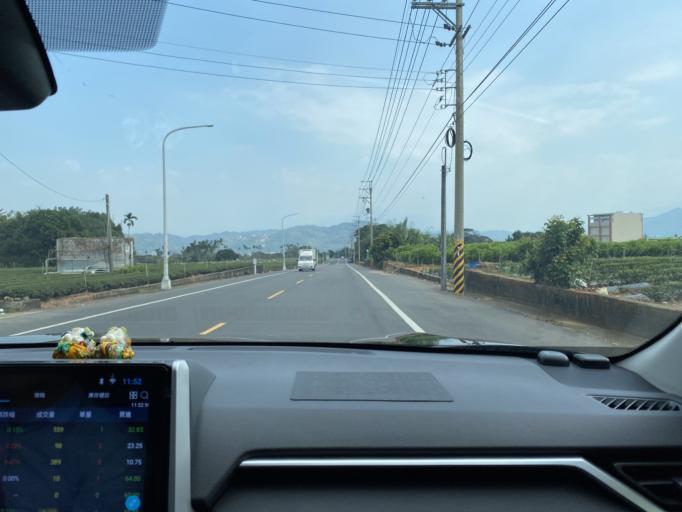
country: TW
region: Taiwan
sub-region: Nantou
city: Nantou
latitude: 23.8377
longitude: 120.6709
